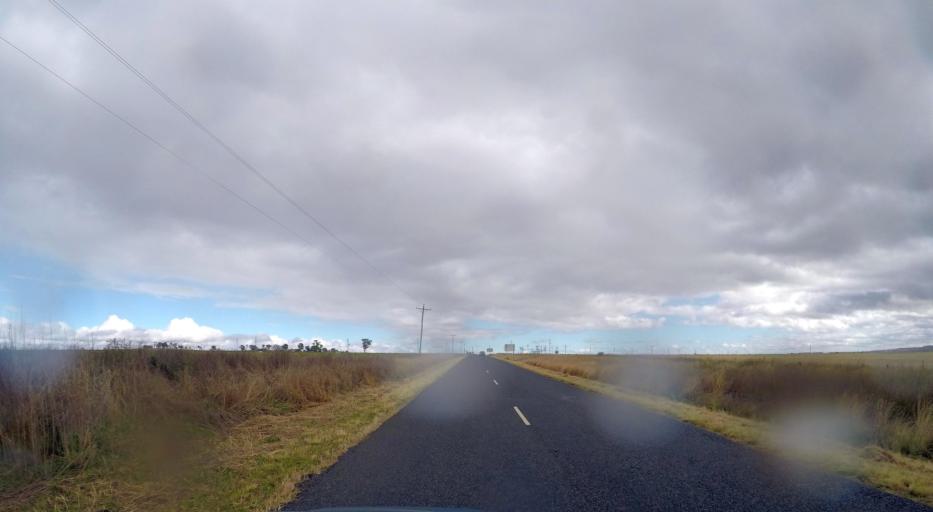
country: AU
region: Queensland
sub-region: Southern Downs
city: Warwick
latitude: -28.0569
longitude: 152.0187
